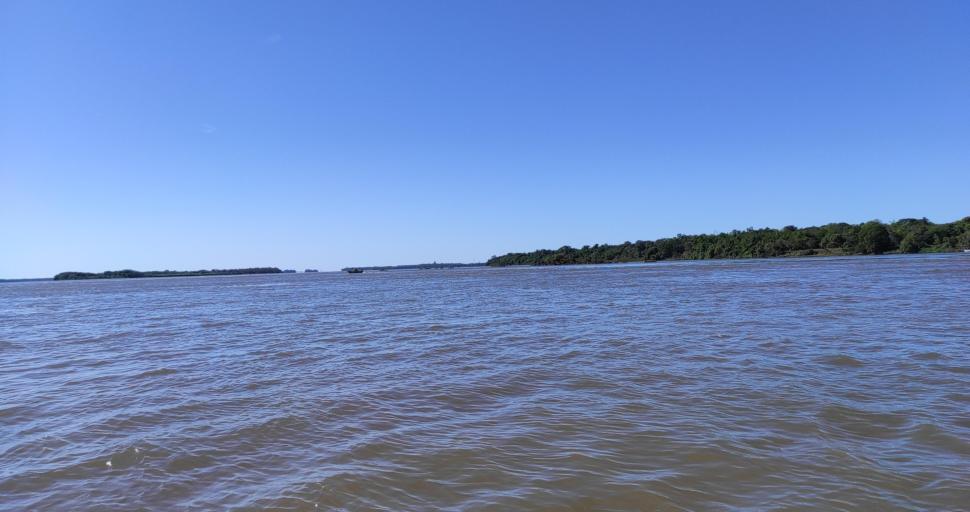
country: AR
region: Corrientes
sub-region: Departamento de Itati
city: Itati
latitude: -27.2786
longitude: -58.3253
